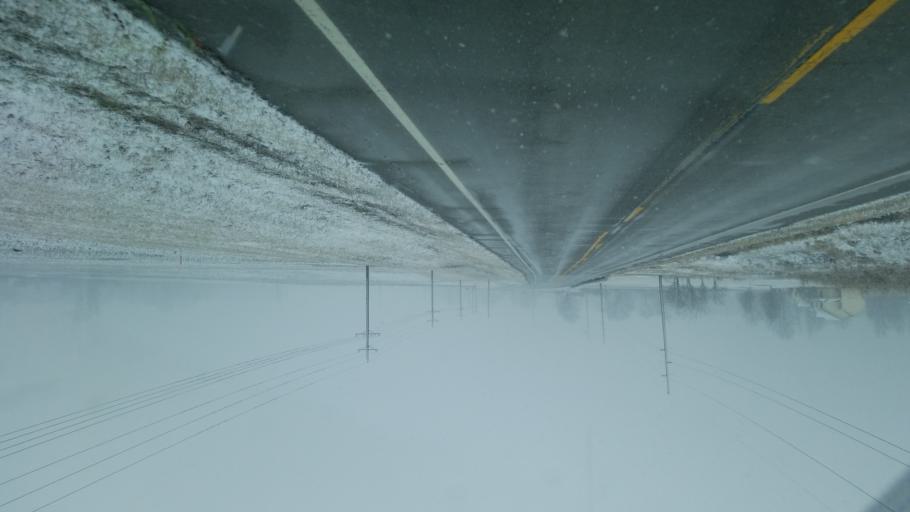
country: US
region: Ohio
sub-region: Champaign County
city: North Lewisburg
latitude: 40.3201
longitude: -83.5218
